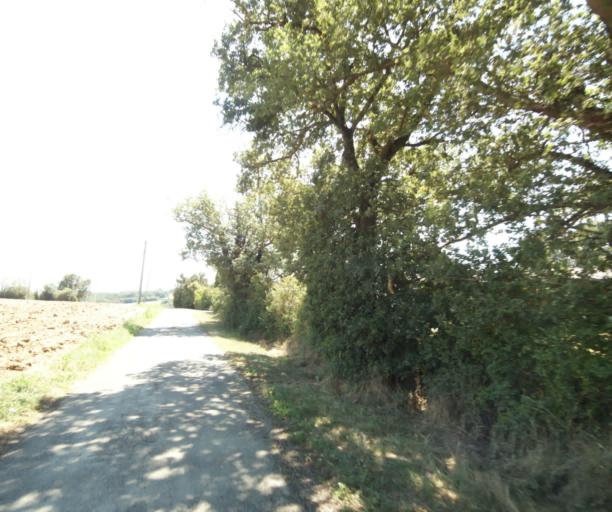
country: FR
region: Midi-Pyrenees
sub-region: Departement de l'Ariege
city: Lezat-sur-Leze
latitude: 43.2470
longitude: 1.3281
